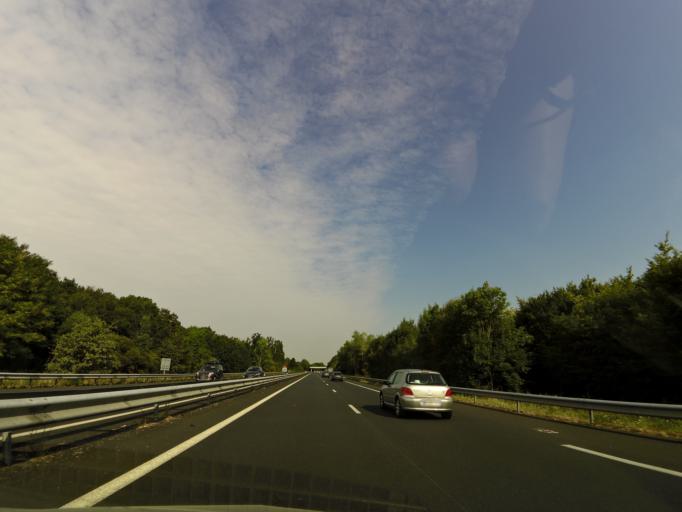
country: FR
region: Pays de la Loire
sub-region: Departement de la Vendee
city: Bouffere
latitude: 46.9403
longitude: -1.3476
